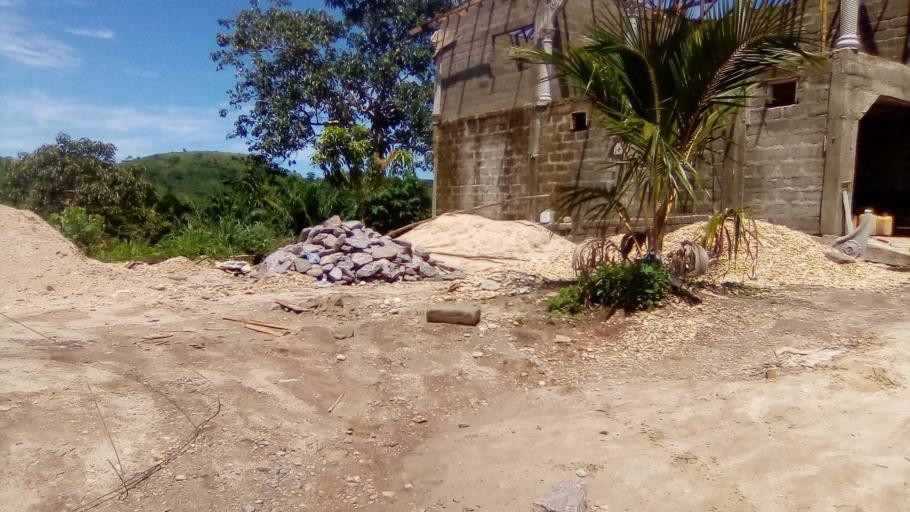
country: SL
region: Eastern Province
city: Simbakoro
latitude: 8.6317
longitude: -10.9952
